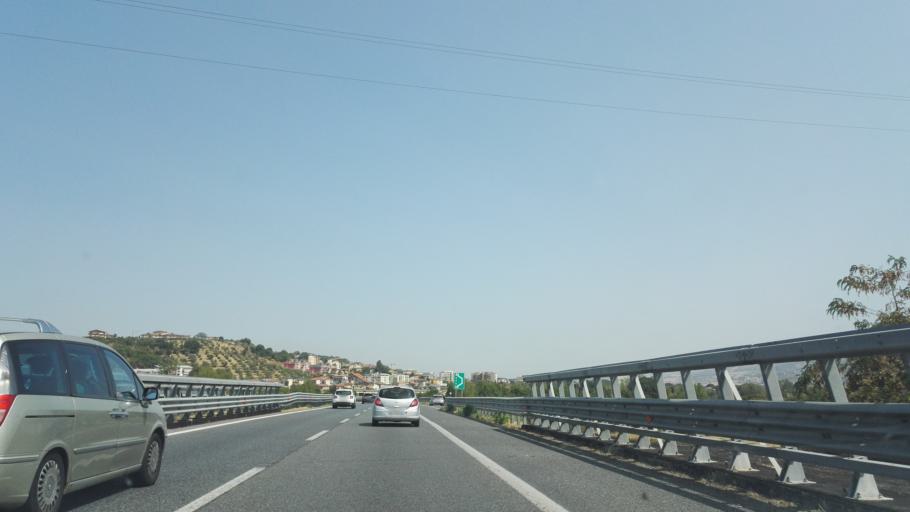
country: IT
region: Calabria
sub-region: Provincia di Cosenza
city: Settimo
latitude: 39.3778
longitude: 16.2366
